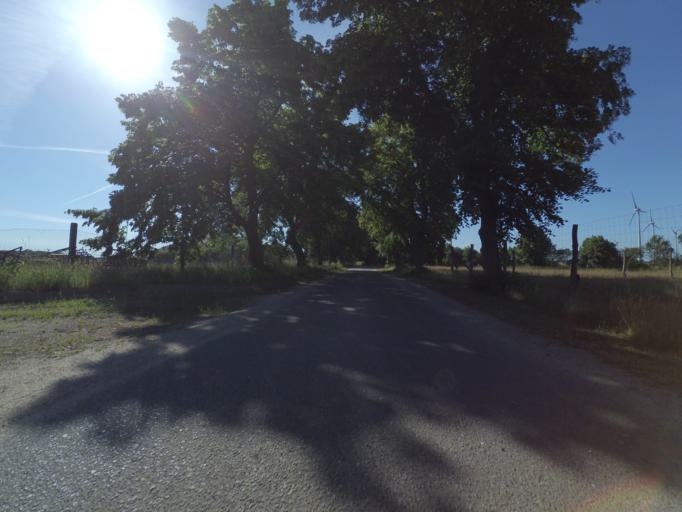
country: DE
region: Mecklenburg-Vorpommern
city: Siggelkow
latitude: 53.3619
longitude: 12.0258
